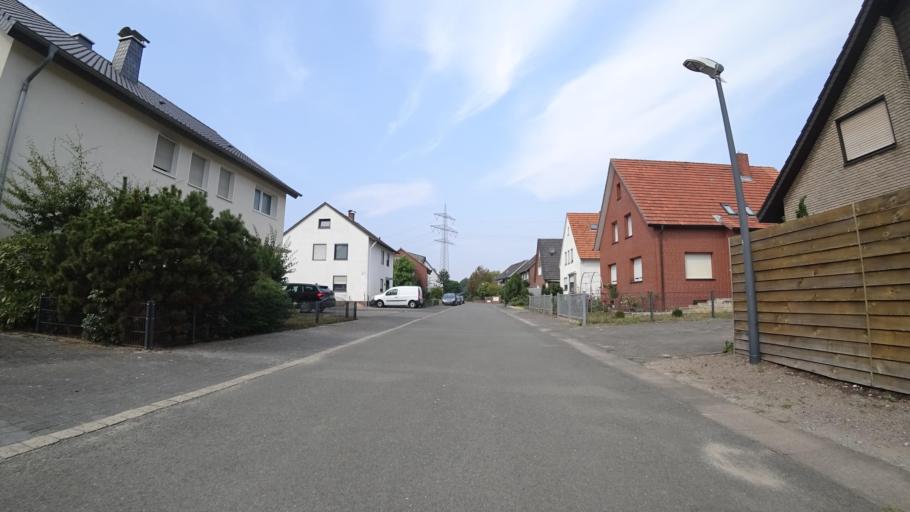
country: DE
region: North Rhine-Westphalia
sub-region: Regierungsbezirk Detmold
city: Guetersloh
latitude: 51.9253
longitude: 8.4377
